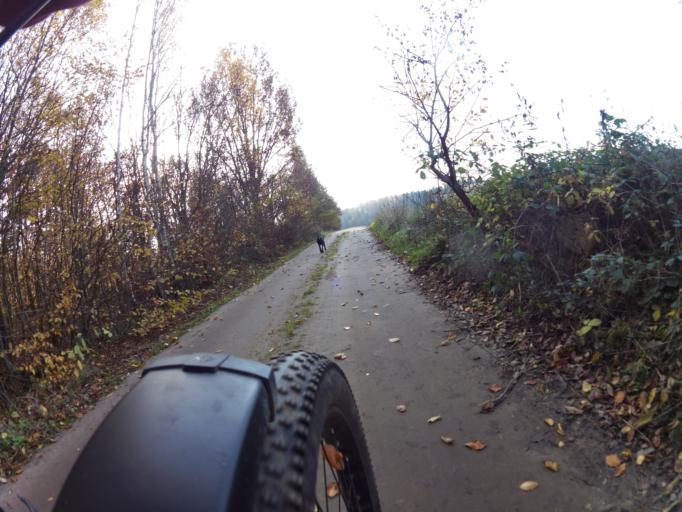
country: PL
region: Pomeranian Voivodeship
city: Strzelno
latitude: 54.7452
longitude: 18.2859
